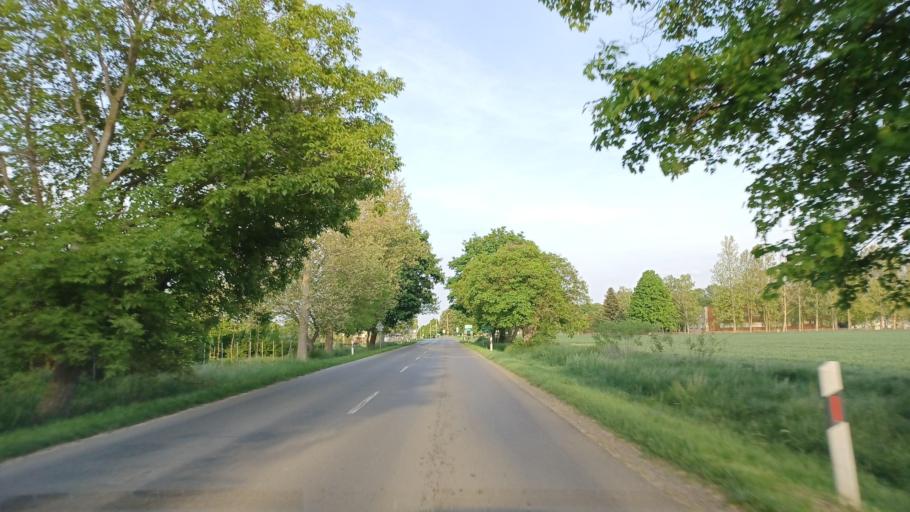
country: HU
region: Baranya
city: Boly
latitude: 45.9867
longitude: 18.5311
